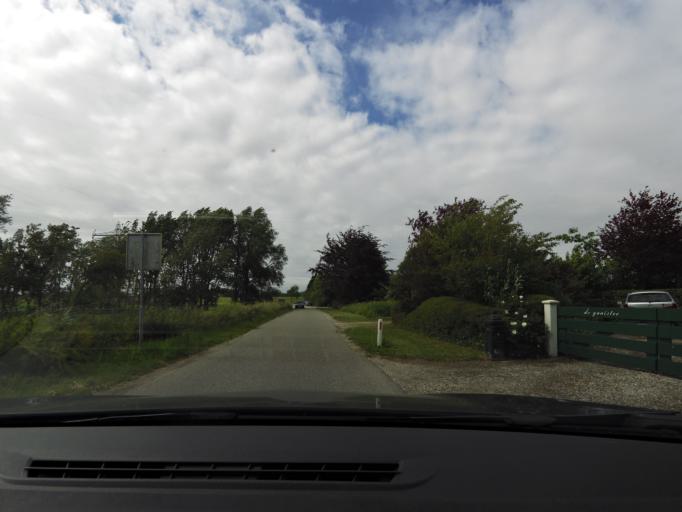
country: NL
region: South Holland
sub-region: Gemeente Brielle
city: Brielle
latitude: 51.9185
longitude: 4.1262
